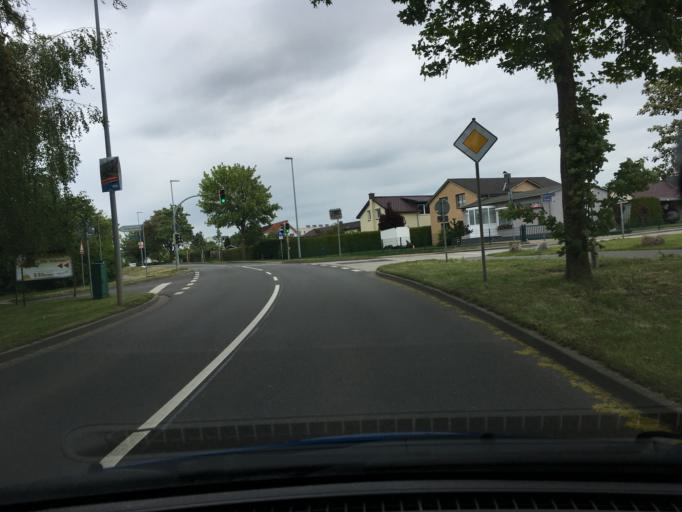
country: DE
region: Mecklenburg-Vorpommern
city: Wismar
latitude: 53.8799
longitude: 11.4300
